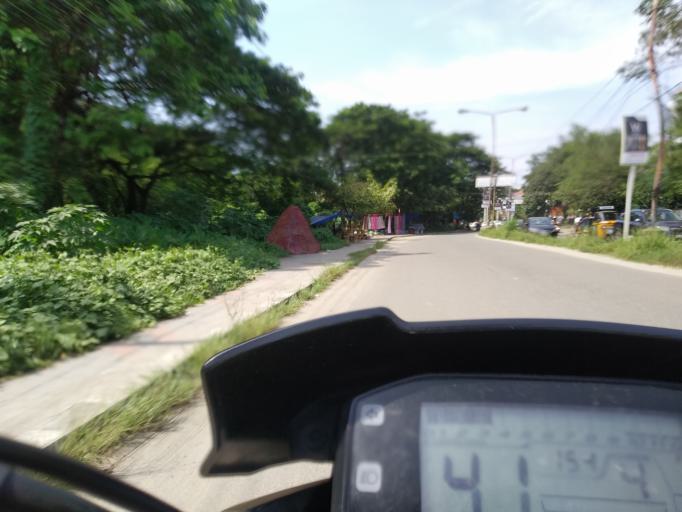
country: IN
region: Kerala
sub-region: Ernakulam
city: Cochin
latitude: 9.9711
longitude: 76.2983
